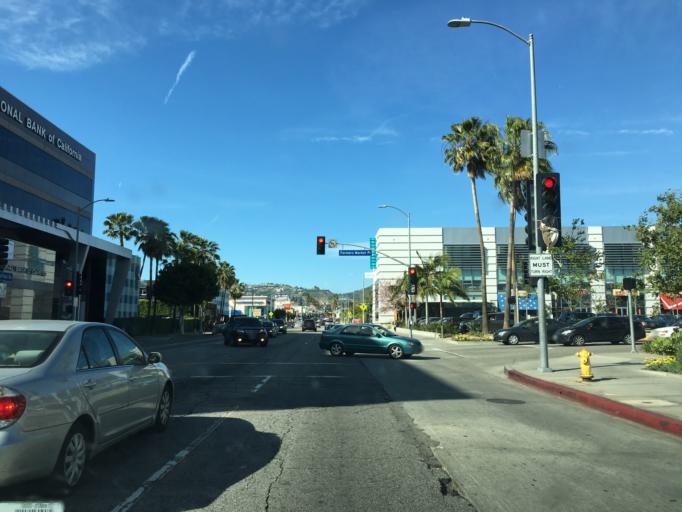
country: US
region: California
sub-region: Los Angeles County
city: West Hollywood
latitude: 34.0727
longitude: -118.3613
